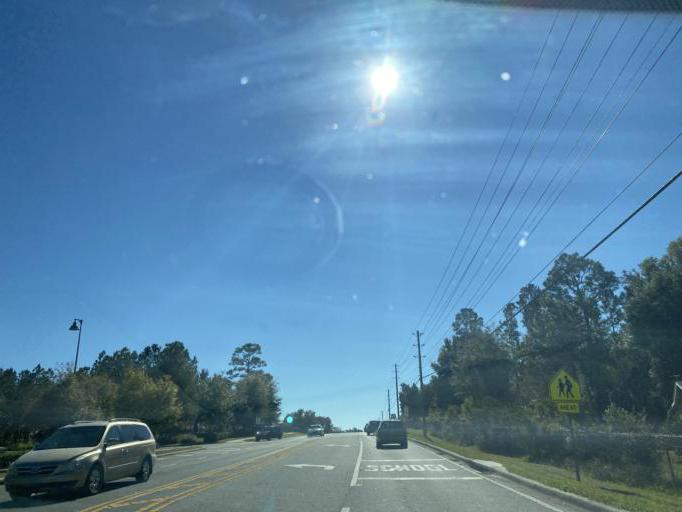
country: US
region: Florida
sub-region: Lake County
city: Lady Lake
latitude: 28.9318
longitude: -81.9370
